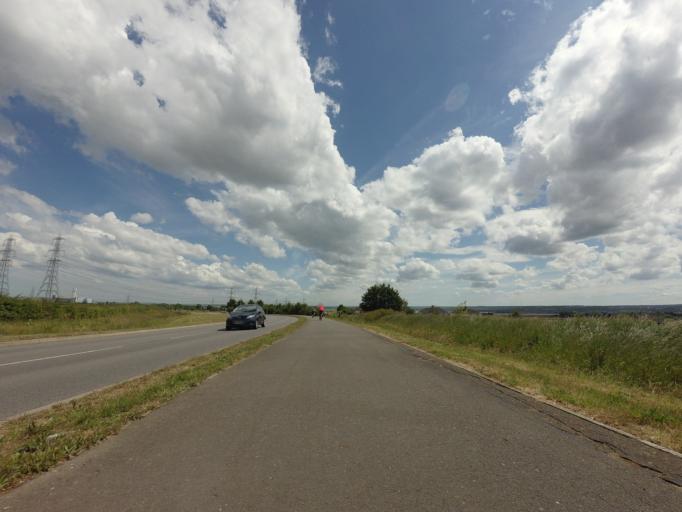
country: GB
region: England
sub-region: Kent
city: Hoo
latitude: 51.4282
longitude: 0.5756
